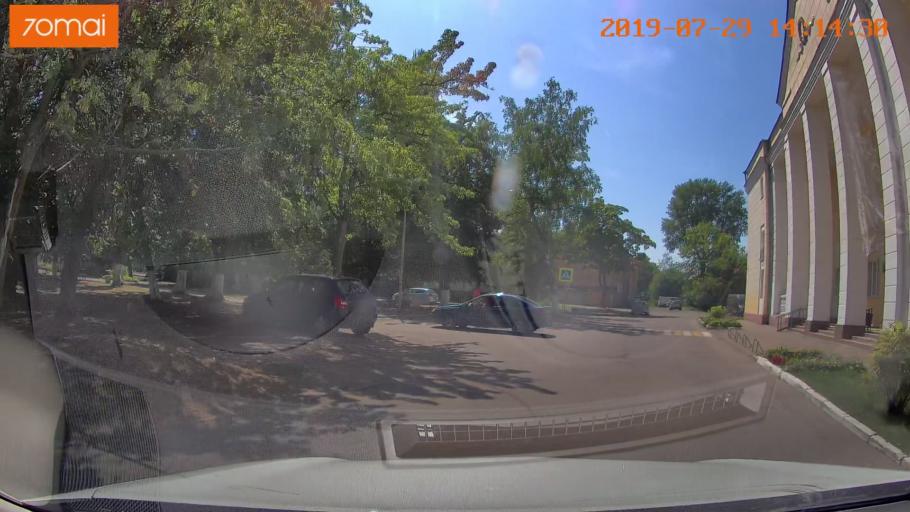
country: RU
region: Kaliningrad
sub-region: Gorod Kaliningrad
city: Baltiysk
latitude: 54.6493
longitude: 19.9020
